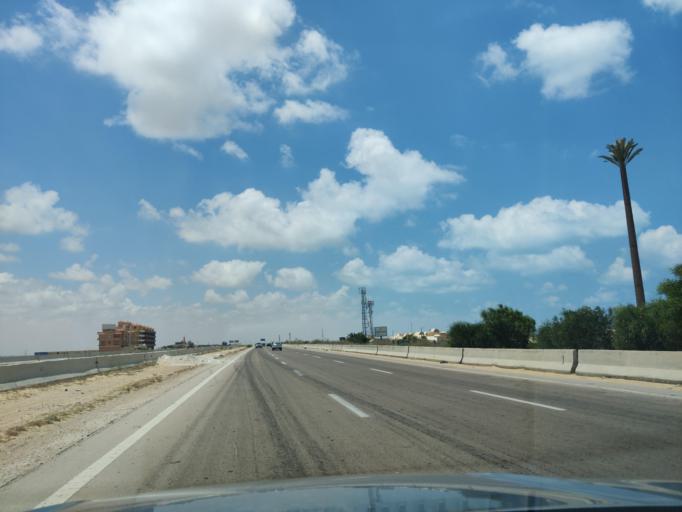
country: EG
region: Muhafazat Matruh
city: Al `Alamayn
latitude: 30.8241
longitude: 29.1863
